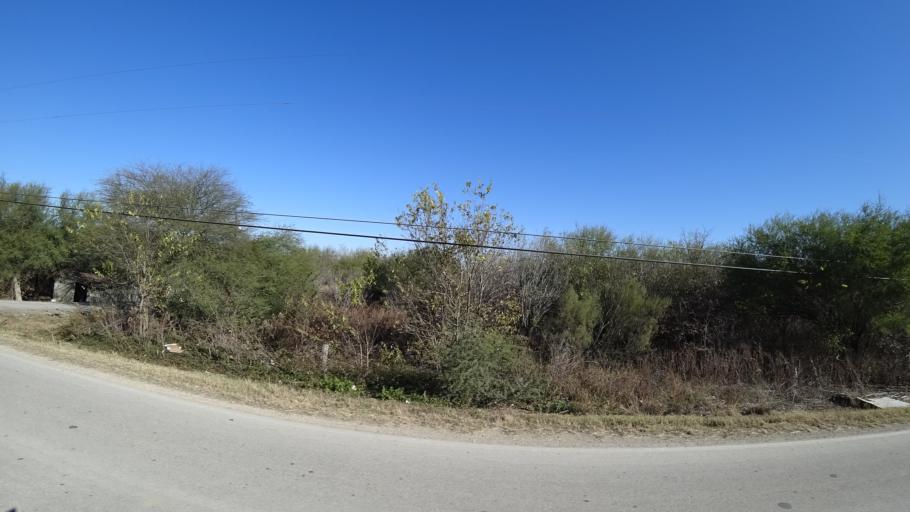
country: US
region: Texas
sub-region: Travis County
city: Onion Creek
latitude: 30.1234
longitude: -97.6713
